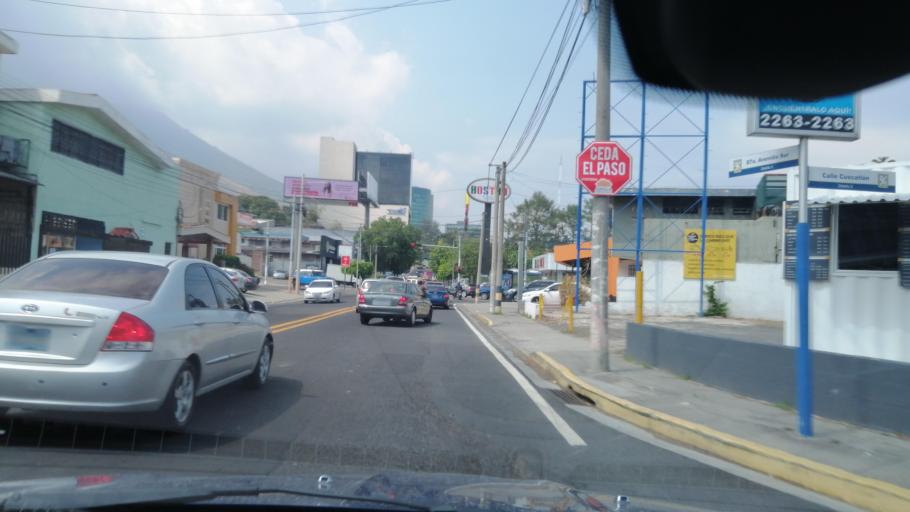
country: SV
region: La Libertad
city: Antiguo Cuscatlan
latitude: 13.7013
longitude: -89.2412
